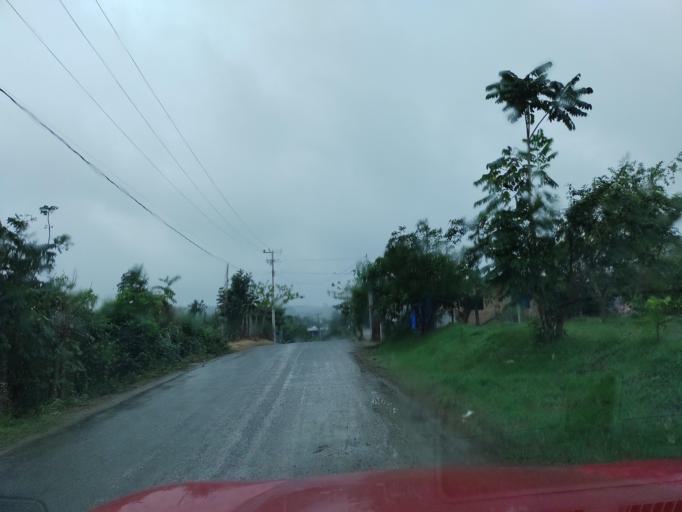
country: MX
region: Veracruz
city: Agua Dulce
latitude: 20.3328
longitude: -97.3261
